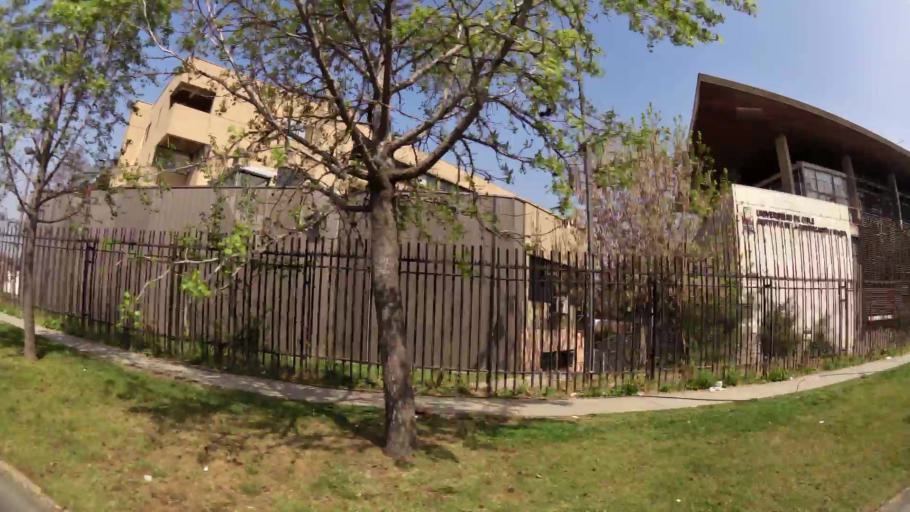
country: CL
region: Santiago Metropolitan
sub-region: Provincia de Santiago
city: Villa Presidente Frei, Nunoa, Santiago, Chile
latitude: -33.4675
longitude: -70.5940
